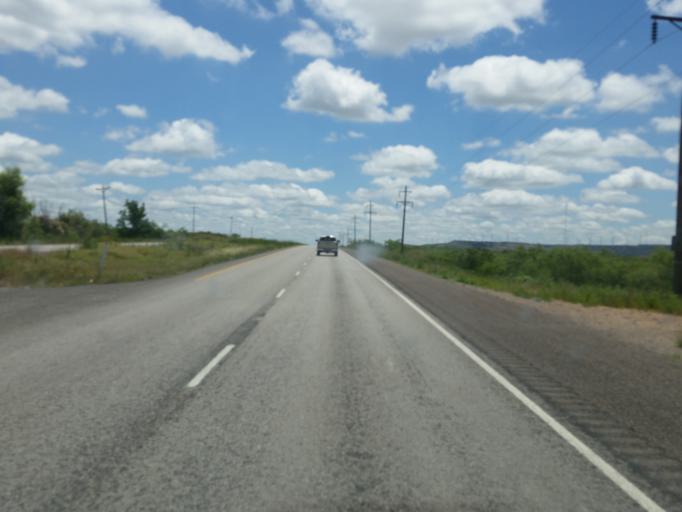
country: US
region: Texas
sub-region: Garza County
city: Post
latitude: 33.0015
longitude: -101.1610
